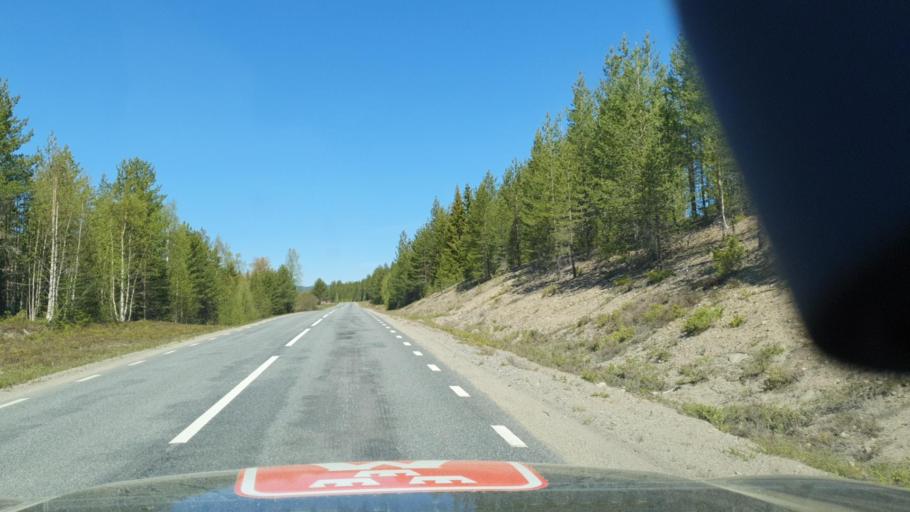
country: SE
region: Vaesternorrland
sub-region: OErnskoeldsviks Kommun
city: Bredbyn
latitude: 63.7386
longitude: 18.5008
